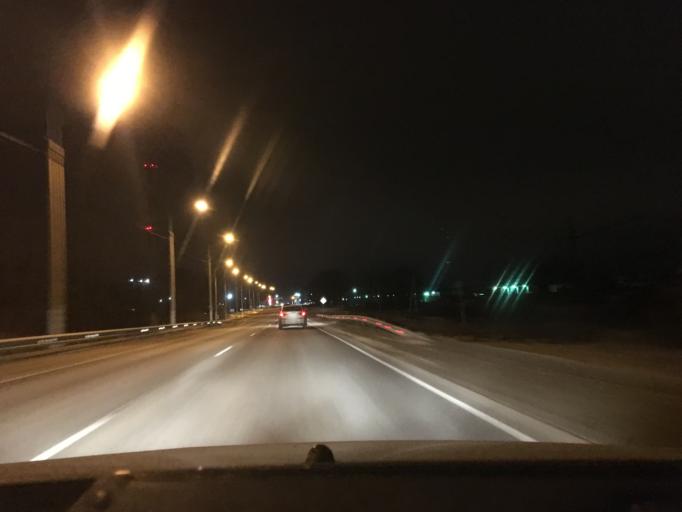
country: RU
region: Tula
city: Pervomayskiy
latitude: 54.0419
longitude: 37.5270
